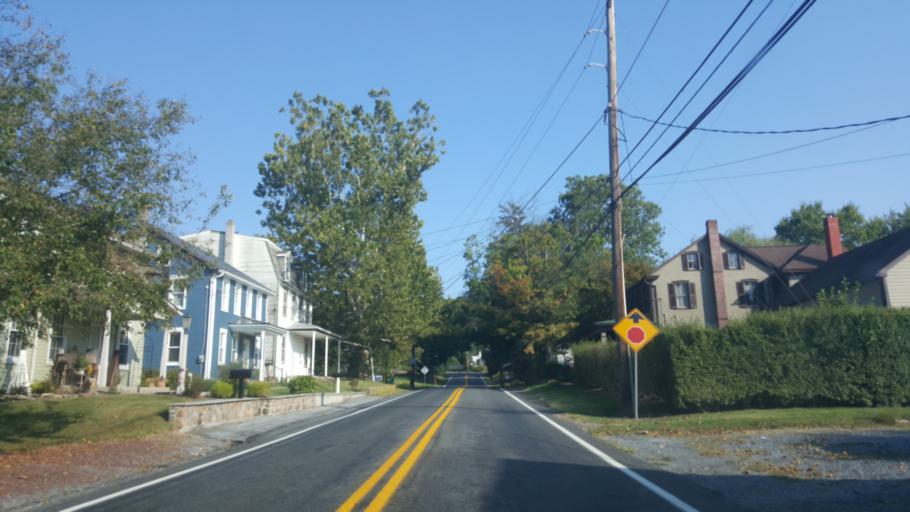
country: US
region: Pennsylvania
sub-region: Lebanon County
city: Campbelltown
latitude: 40.2218
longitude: -76.5404
